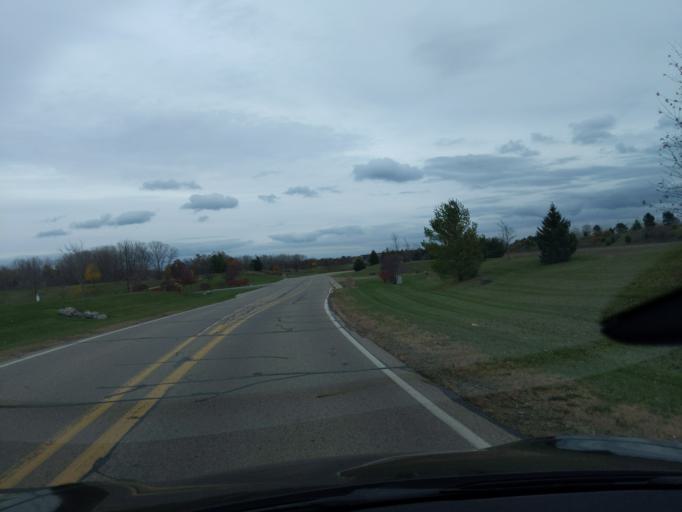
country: US
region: Michigan
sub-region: Ingham County
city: Lansing
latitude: 42.7821
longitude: -84.5293
